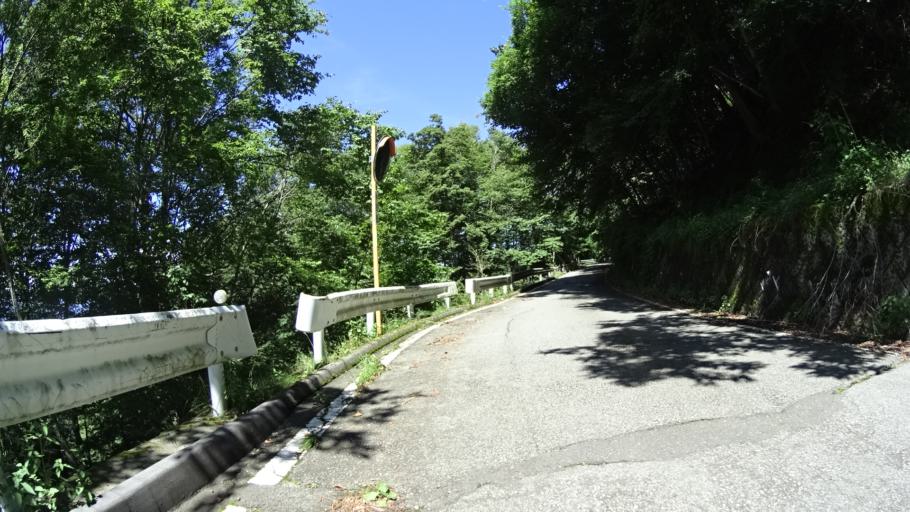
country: JP
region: Yamanashi
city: Enzan
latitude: 35.7373
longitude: 138.8320
